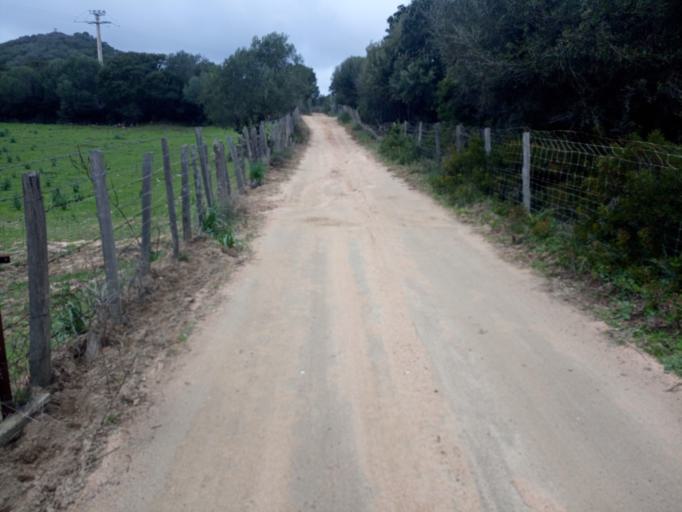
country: FR
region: Corsica
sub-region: Departement de la Corse-du-Sud
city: Sartene
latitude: 41.5480
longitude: 8.8914
